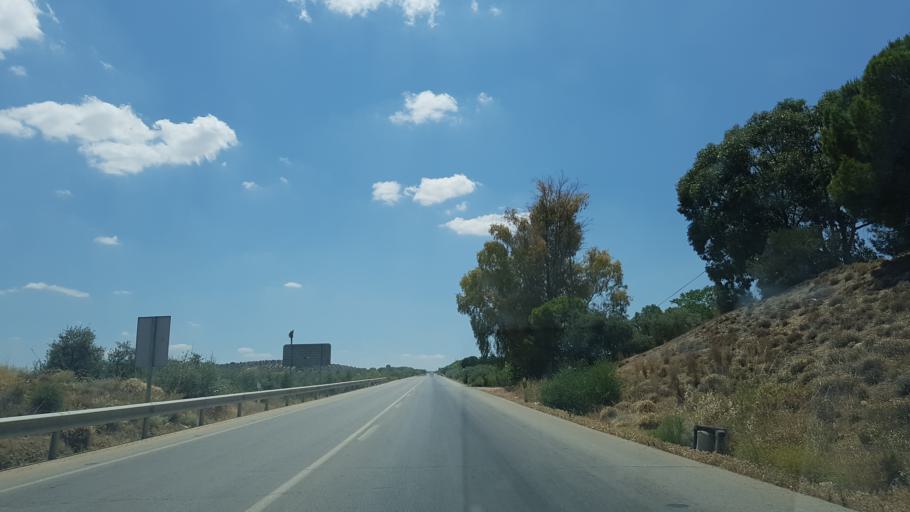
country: ES
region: Andalusia
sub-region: Province of Cordoba
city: Puente-Genil
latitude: 37.3988
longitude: -4.7806
